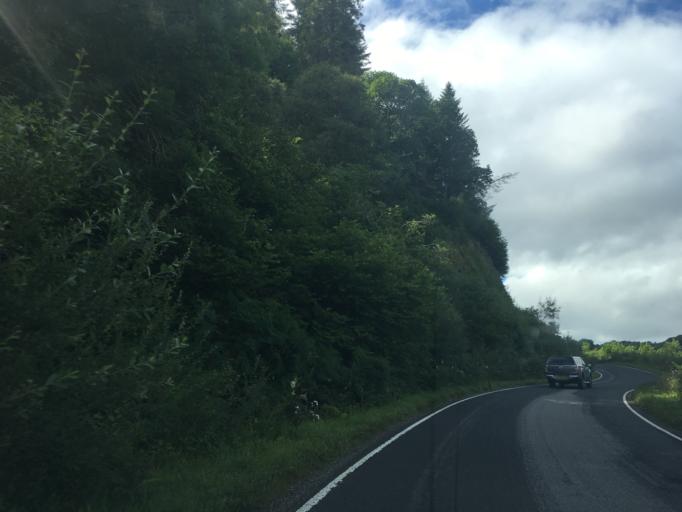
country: GB
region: Scotland
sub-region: Argyll and Bute
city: Ardrishaig
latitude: 56.0783
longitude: -5.5449
